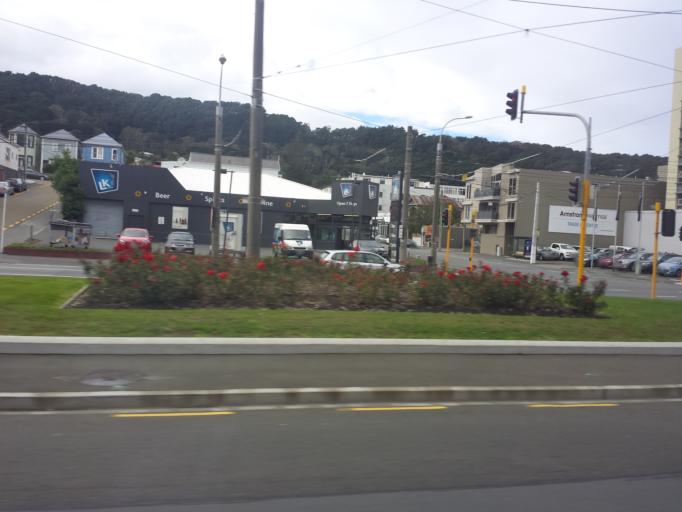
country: NZ
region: Wellington
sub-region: Wellington City
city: Wellington
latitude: -41.2954
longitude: 174.7829
